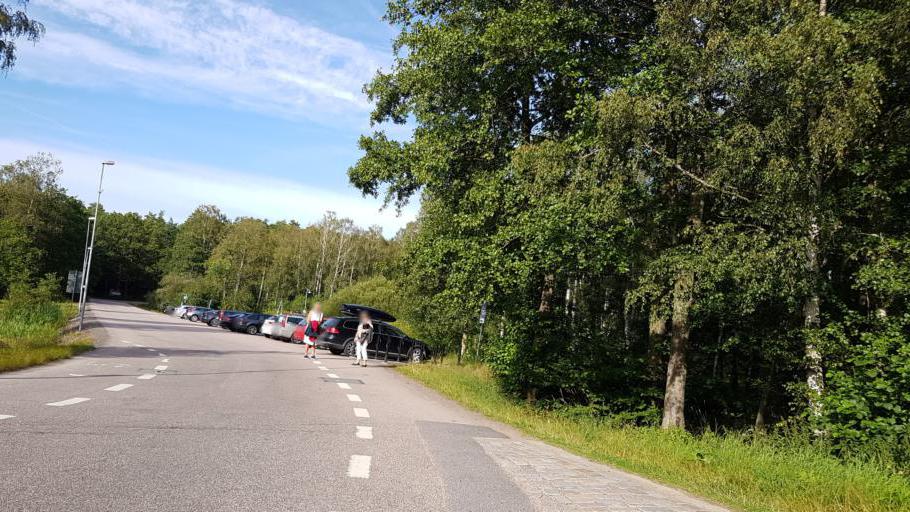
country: SE
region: Vaestra Goetaland
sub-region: Molndal
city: Moelndal
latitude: 57.6604
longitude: 12.0575
